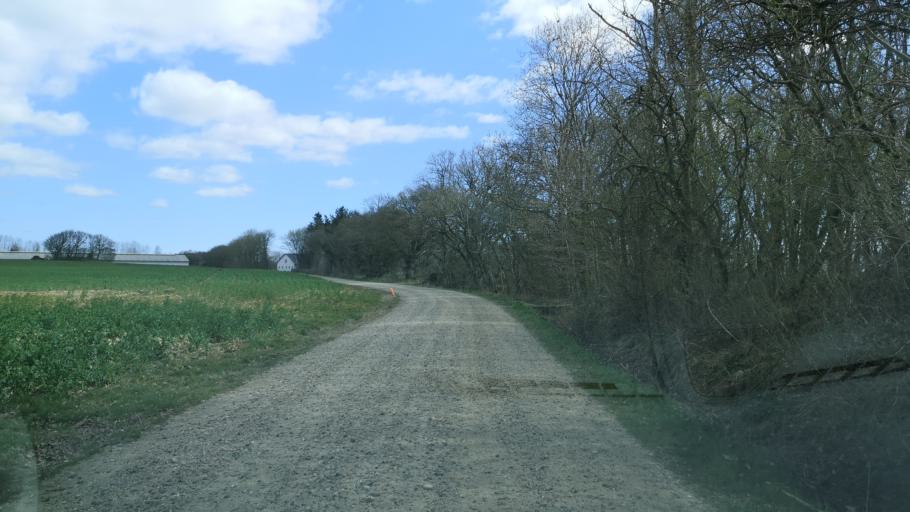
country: DK
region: Central Jutland
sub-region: Ringkobing-Skjern Kommune
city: Skjern
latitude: 55.9705
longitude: 8.4999
